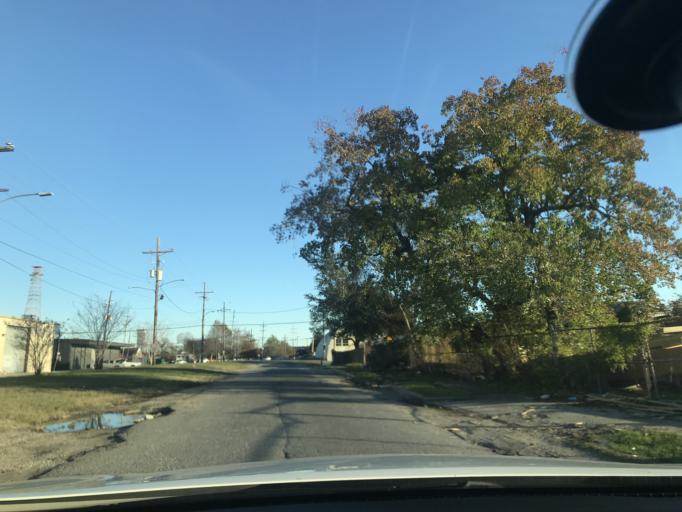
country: US
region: Louisiana
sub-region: Orleans Parish
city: New Orleans
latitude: 29.9551
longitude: -90.1043
